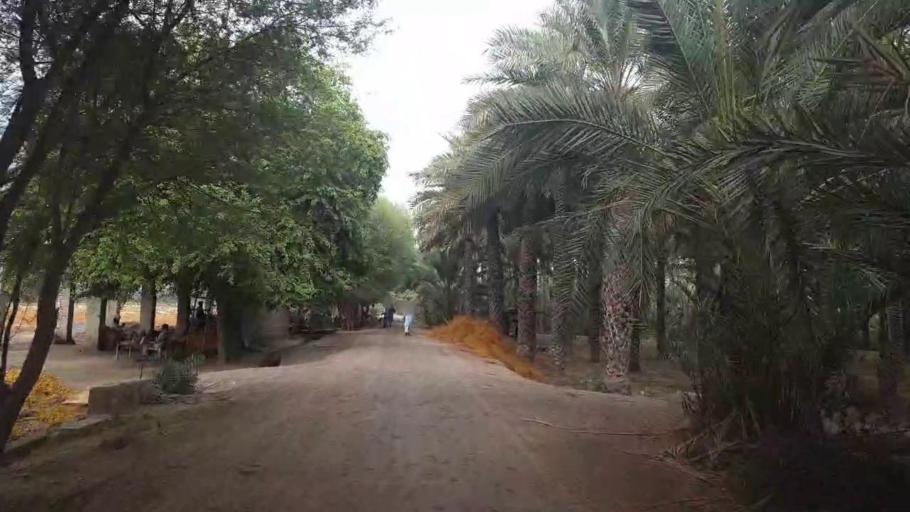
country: PK
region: Sindh
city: Sukkur
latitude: 27.6425
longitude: 68.8196
